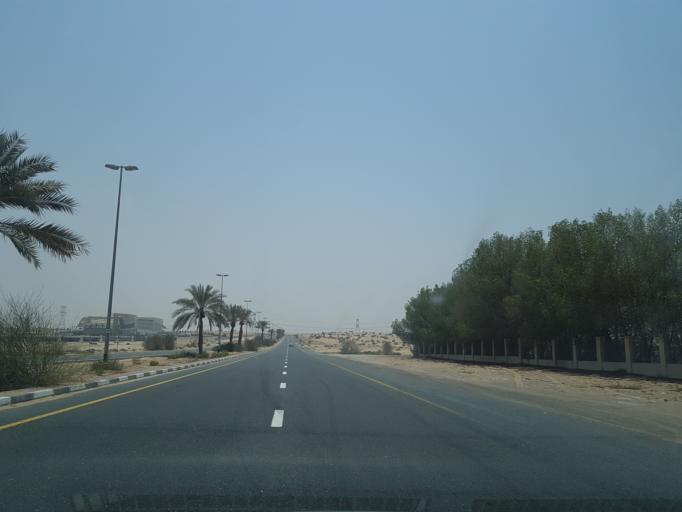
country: AE
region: Ash Shariqah
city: Sharjah
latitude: 25.1107
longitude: 55.4082
